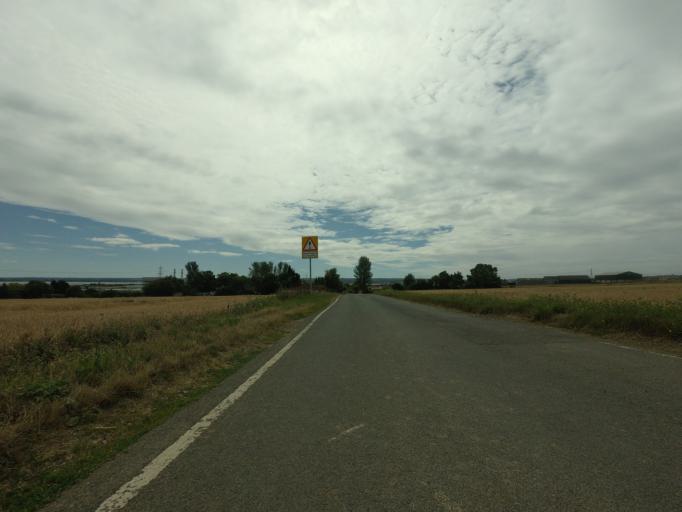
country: GB
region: England
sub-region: Medway
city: Stoke
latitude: 51.4376
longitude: 0.5979
